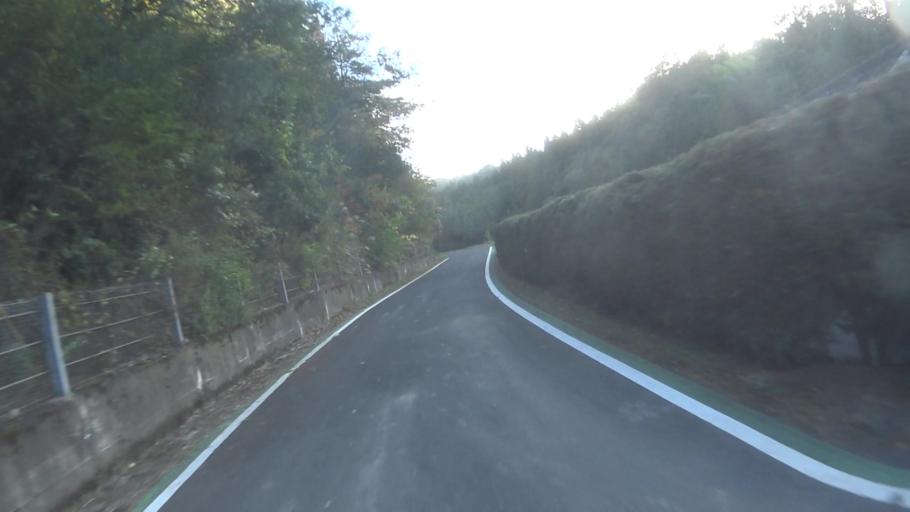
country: JP
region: Kyoto
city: Ayabe
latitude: 35.2777
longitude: 135.2497
